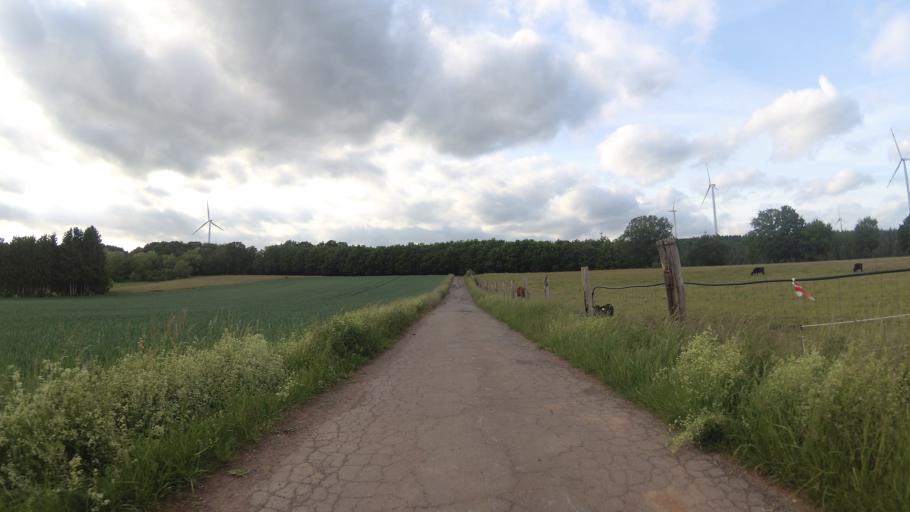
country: DE
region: Saarland
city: Hangard
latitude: 49.4236
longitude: 7.2068
